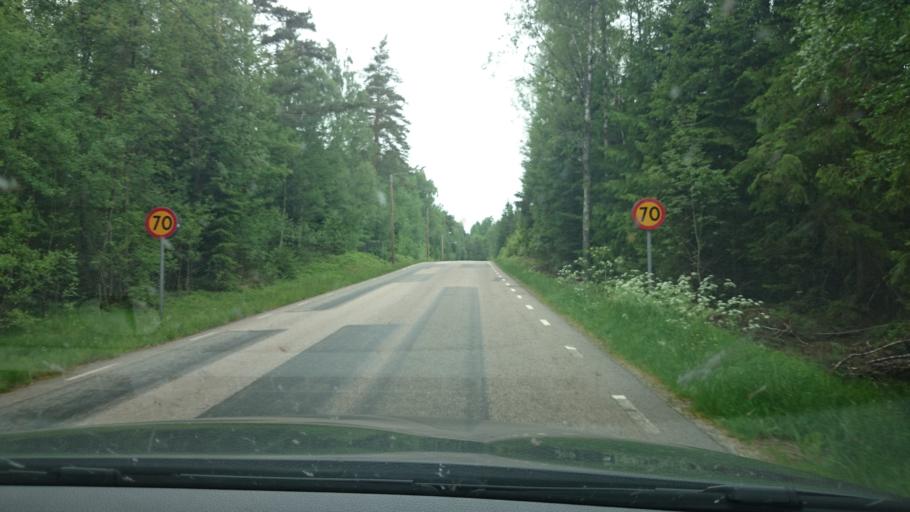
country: SE
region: Halland
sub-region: Hylte Kommun
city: Torup
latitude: 56.9660
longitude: 13.1444
